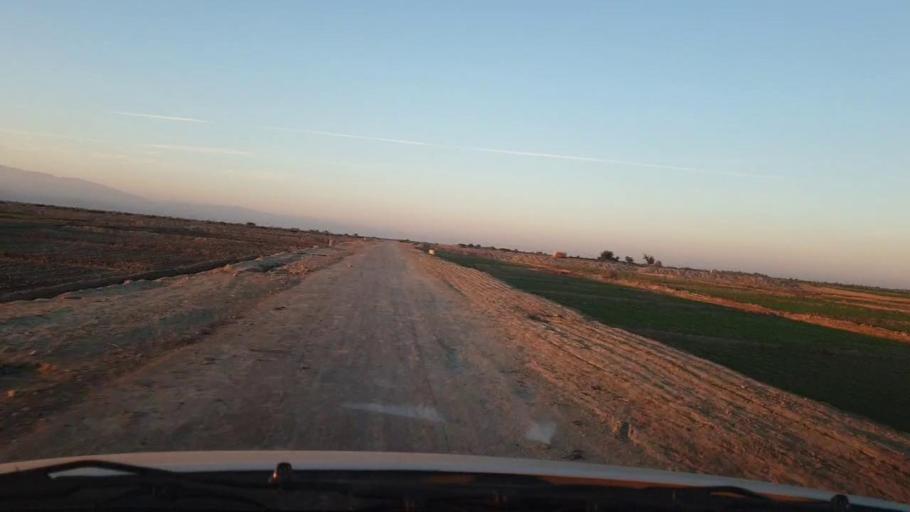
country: PK
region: Sindh
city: Johi
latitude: 26.8382
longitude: 67.4413
